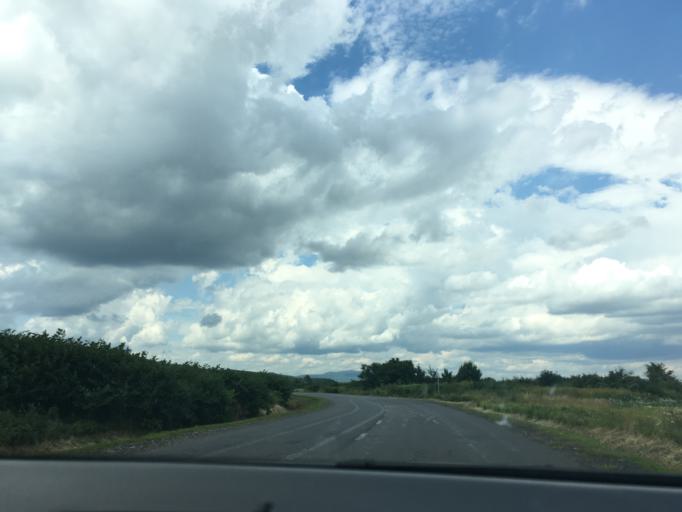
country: HU
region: Borsod-Abauj-Zemplen
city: Satoraljaujhely
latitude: 48.4113
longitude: 21.6535
